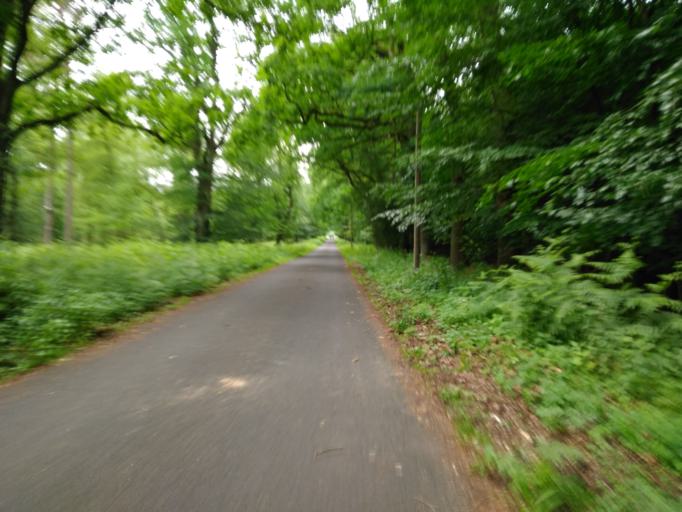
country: DE
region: North Rhine-Westphalia
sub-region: Regierungsbezirk Dusseldorf
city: Hunxe
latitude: 51.6344
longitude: 6.8335
